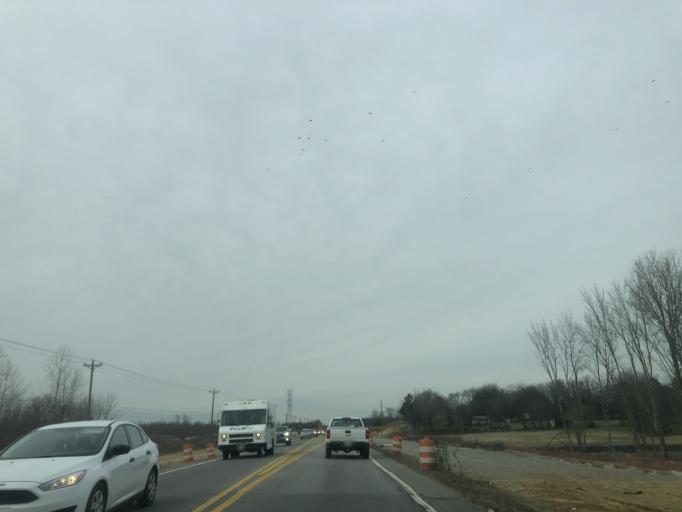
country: US
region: Tennessee
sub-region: Wilson County
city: Mount Juliet
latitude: 36.2432
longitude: -86.4328
